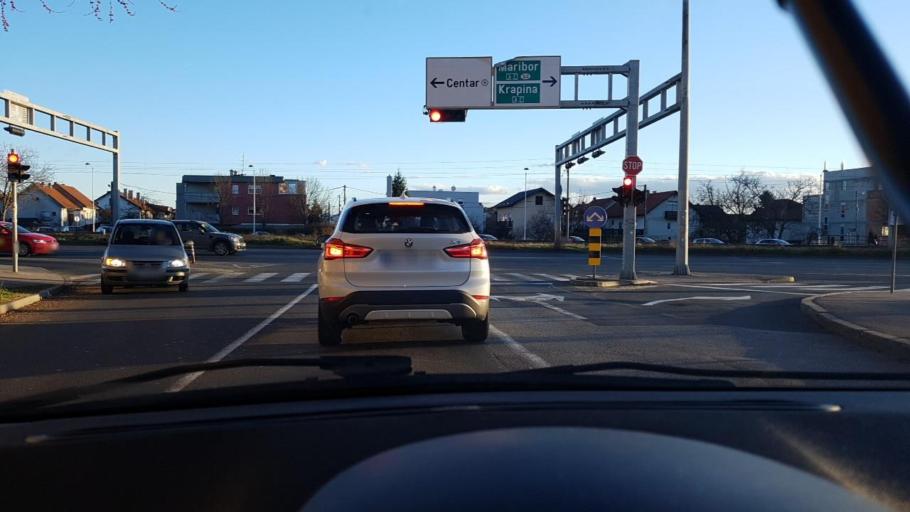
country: HR
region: Grad Zagreb
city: Stenjevec
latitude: 45.8128
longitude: 15.8986
